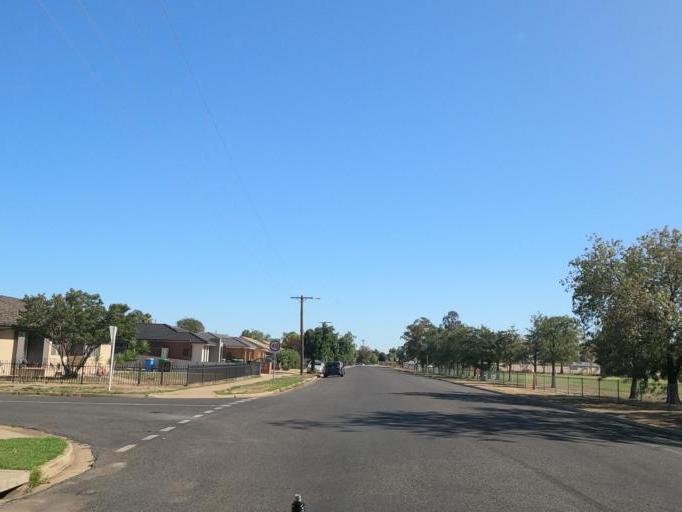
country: AU
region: Victoria
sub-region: Moira
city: Yarrawonga
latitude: -36.0211
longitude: 146.0054
